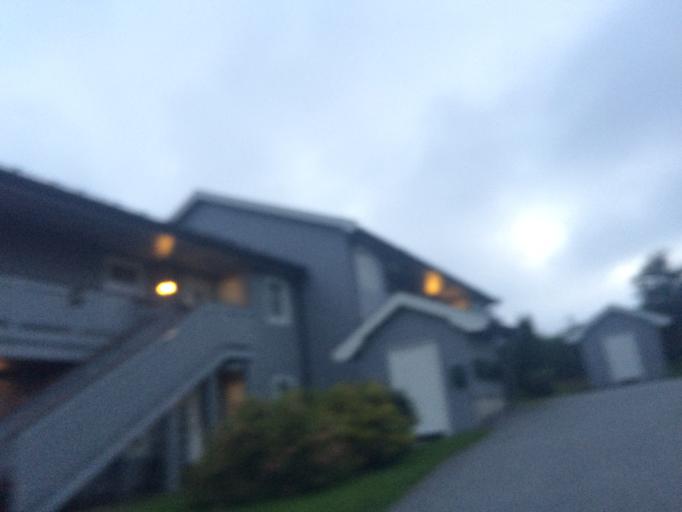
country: NO
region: Akershus
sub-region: Ski
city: Ski
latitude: 59.7183
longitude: 10.8281
